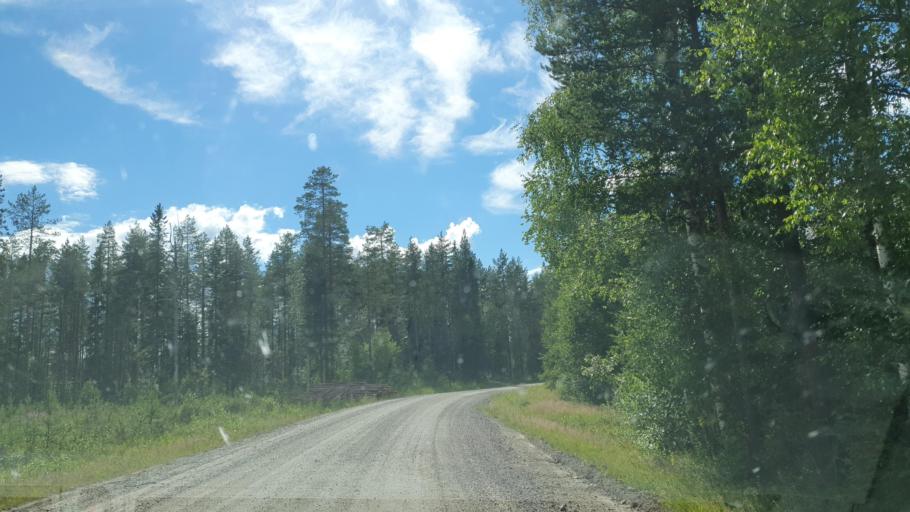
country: FI
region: Kainuu
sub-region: Kehys-Kainuu
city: Kuhmo
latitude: 64.1612
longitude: 29.8345
